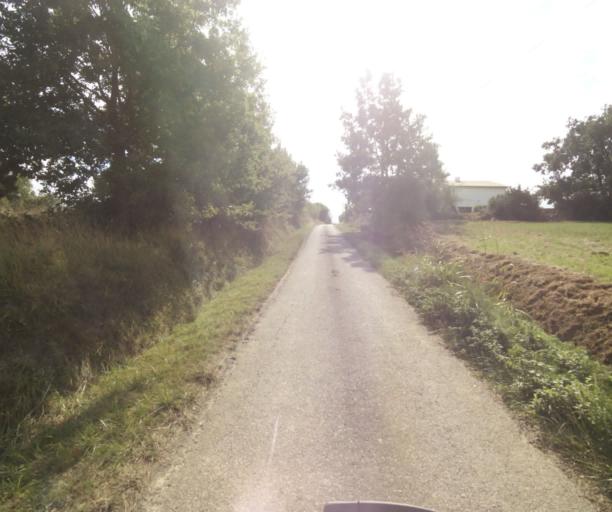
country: FR
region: Midi-Pyrenees
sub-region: Departement du Tarn-et-Garonne
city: Verdun-sur-Garonne
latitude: 43.8634
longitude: 1.1803
